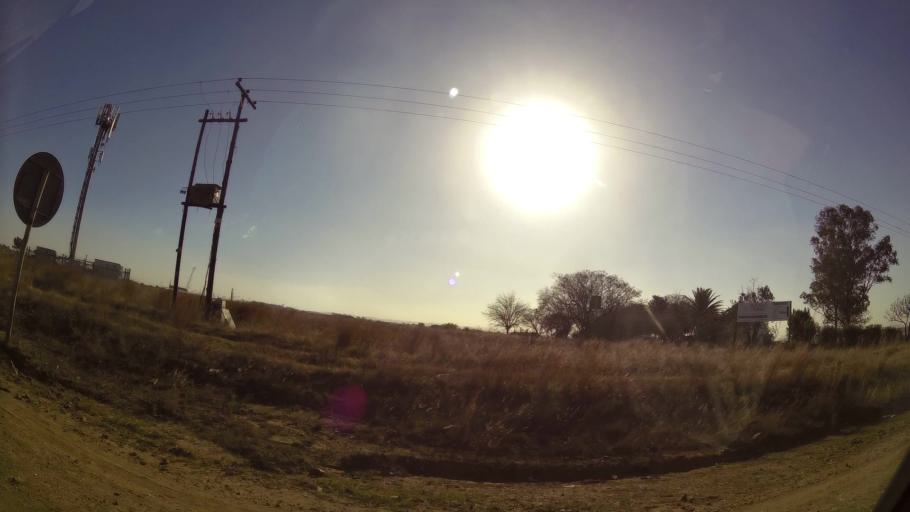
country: ZA
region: Gauteng
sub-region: City of Johannesburg Metropolitan Municipality
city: Diepsloot
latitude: -25.9598
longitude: 27.9570
